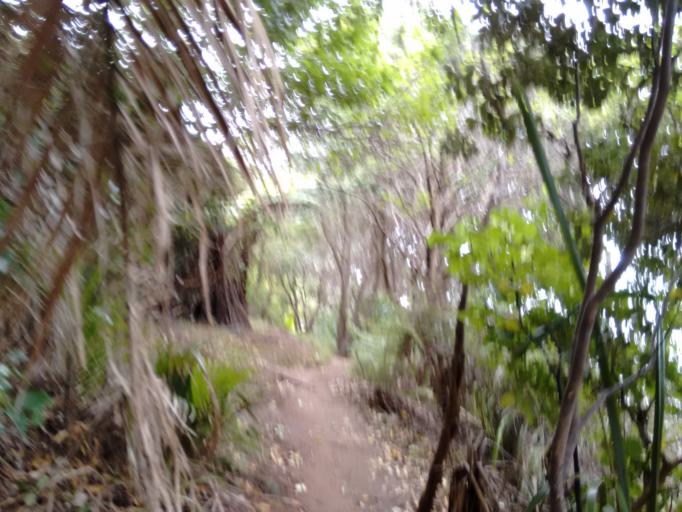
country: NZ
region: Waikato
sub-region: Thames-Coromandel District
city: Coromandel
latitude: -36.7022
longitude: 175.6116
